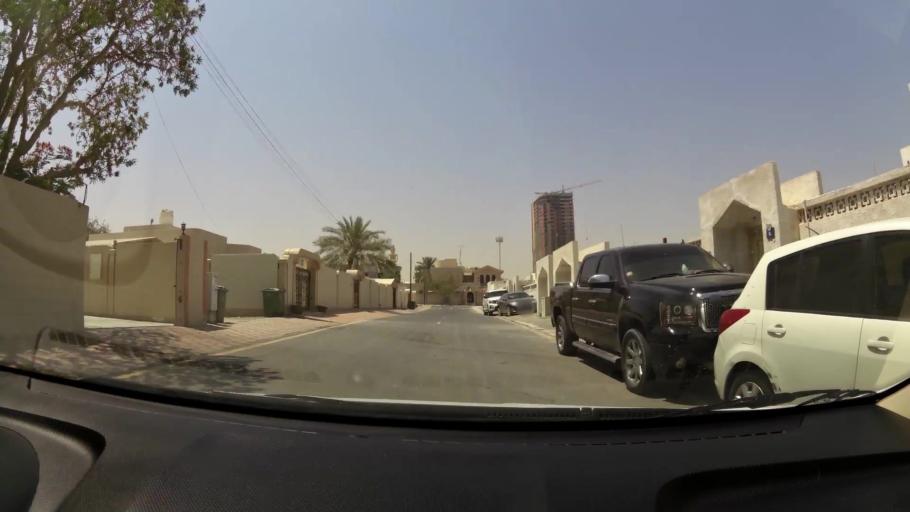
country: AE
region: Ajman
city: Ajman
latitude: 25.4019
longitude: 55.5130
